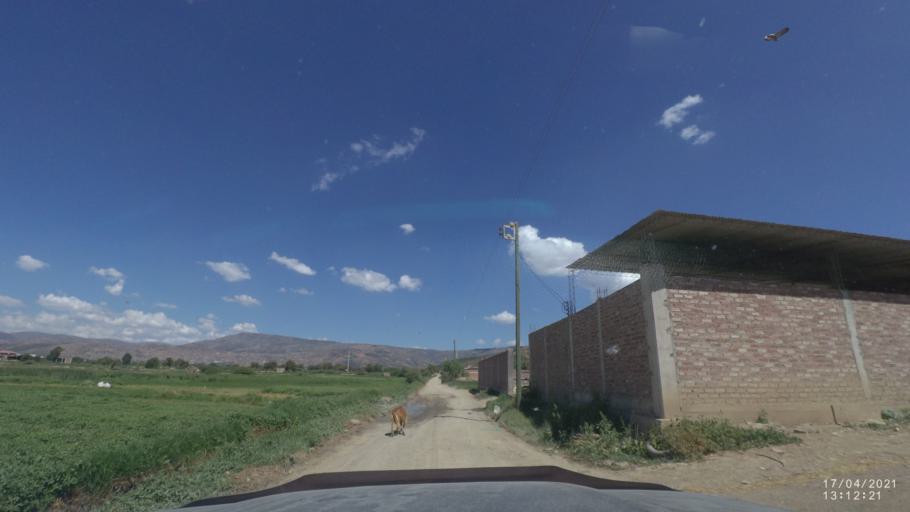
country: BO
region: Cochabamba
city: Cochabamba
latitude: -17.4184
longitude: -66.2216
